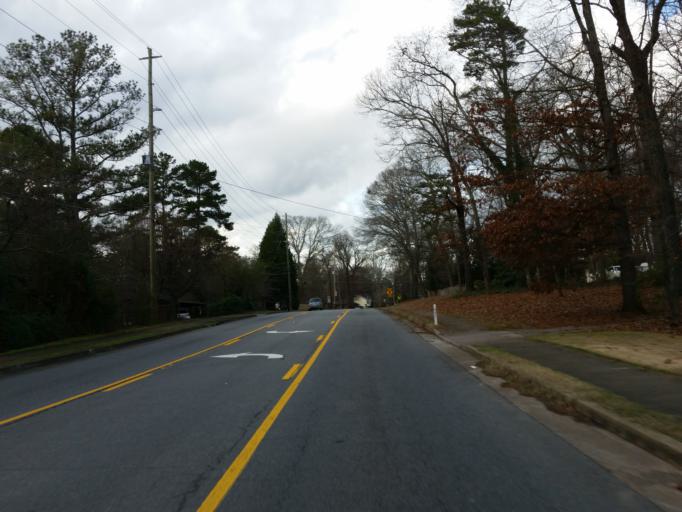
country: US
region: Georgia
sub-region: Cobb County
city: Fair Oaks
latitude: 33.9401
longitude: -84.4922
